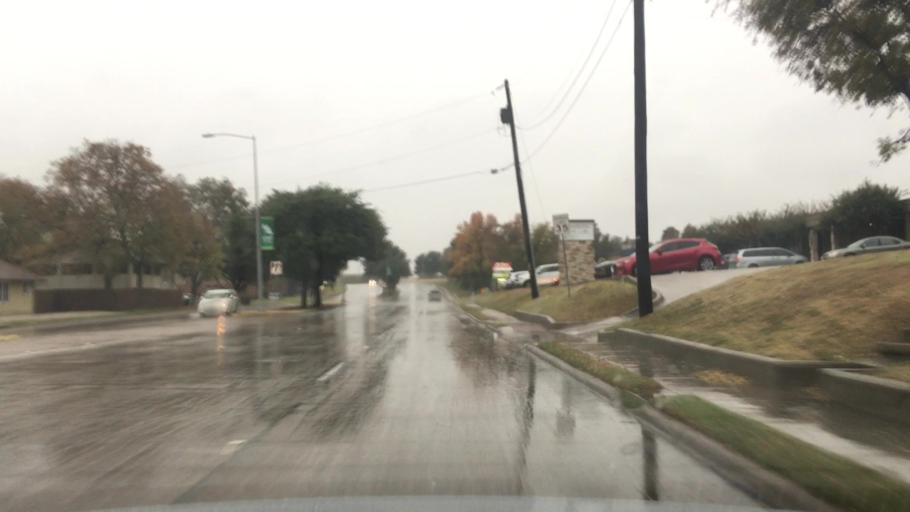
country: US
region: Texas
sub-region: Denton County
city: Denton
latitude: 33.2119
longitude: -97.1374
